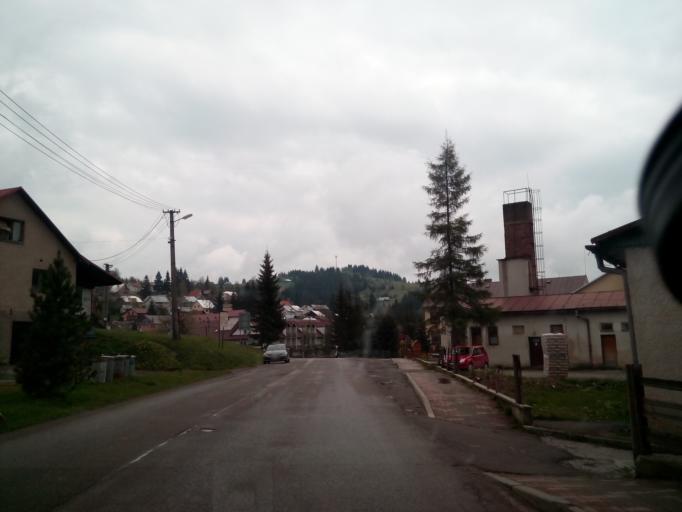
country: SK
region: Zilinsky
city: Oravska Lesna
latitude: 49.3659
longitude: 19.1834
